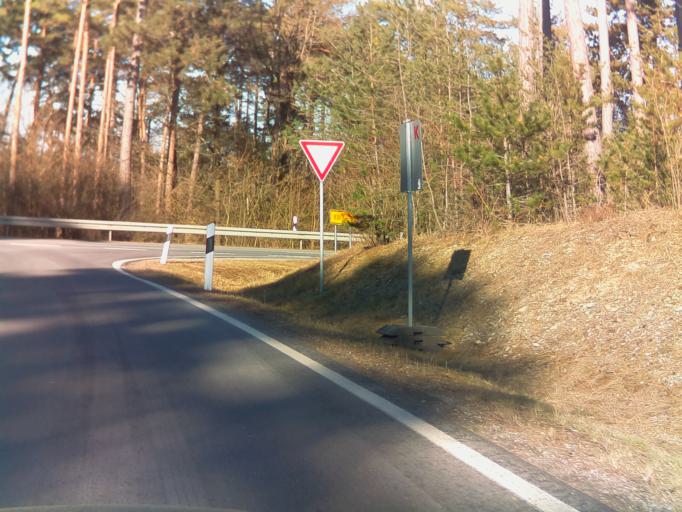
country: DE
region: Bavaria
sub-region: Regierungsbezirk Unterfranken
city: Munnerstadt
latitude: 50.2393
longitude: 10.1789
